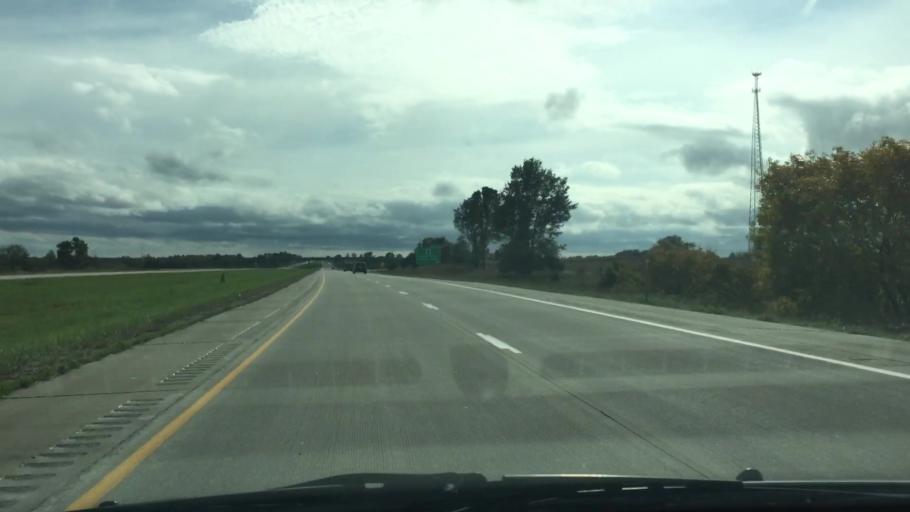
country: US
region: Iowa
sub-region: Decatur County
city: Leon
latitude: 40.8184
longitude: -93.8244
